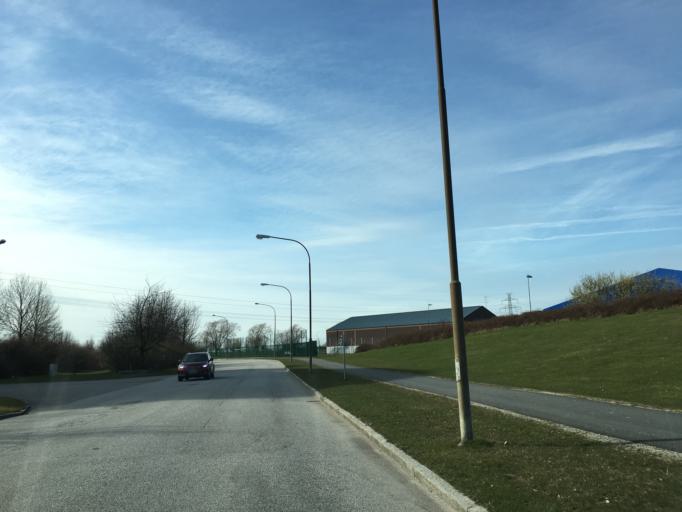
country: SE
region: Skane
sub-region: Lunds Kommun
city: Lund
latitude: 55.7220
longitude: 13.1547
